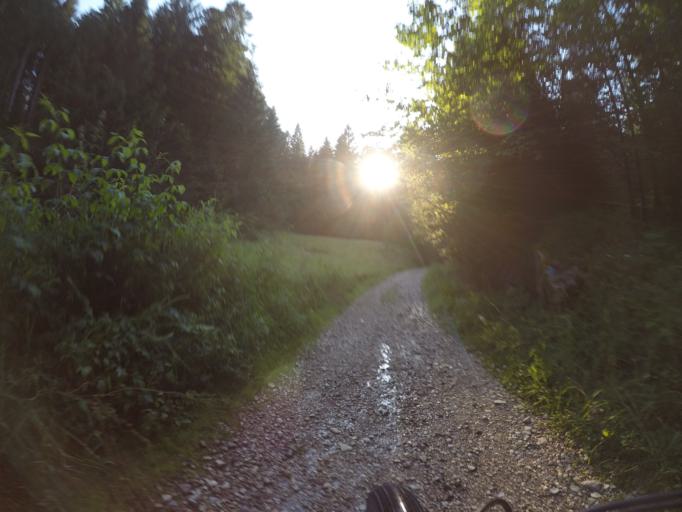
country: IT
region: Veneto
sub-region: Provincia di Vicenza
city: Asiago
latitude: 45.8528
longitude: 11.5163
